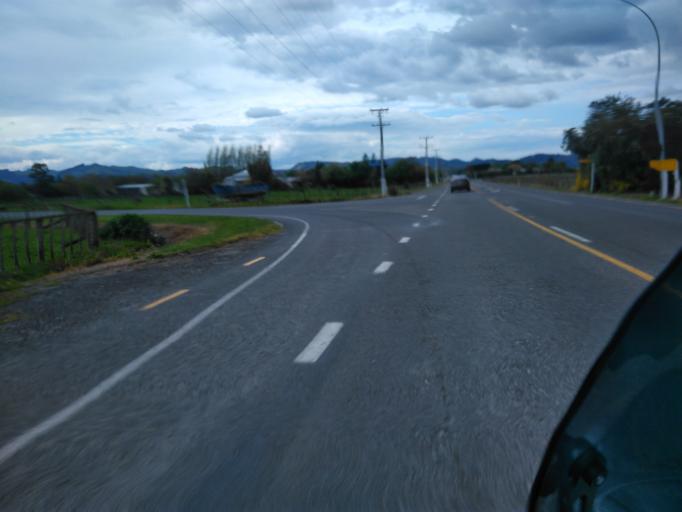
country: NZ
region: Gisborne
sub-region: Gisborne District
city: Gisborne
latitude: -38.6546
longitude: 177.9535
